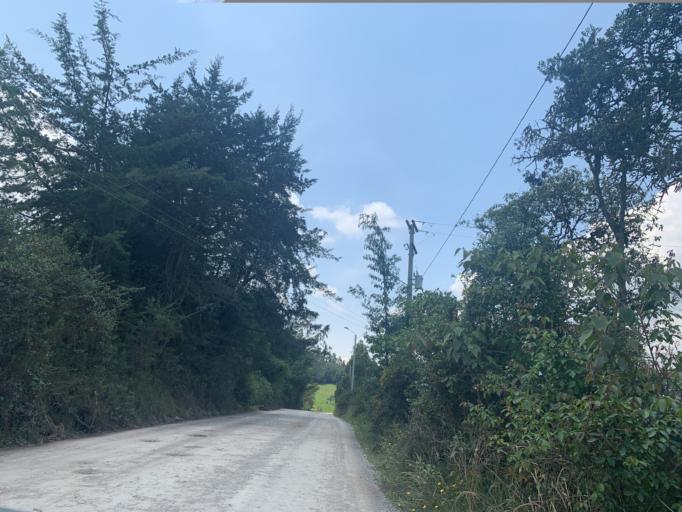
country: CO
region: Boyaca
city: Chiquinquira
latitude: 5.5938
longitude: -73.7595
